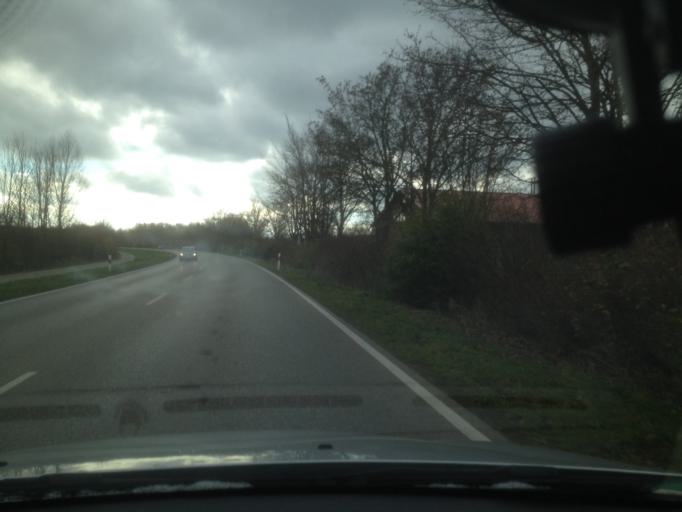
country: DE
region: Bavaria
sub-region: Swabia
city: Mering
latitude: 48.2647
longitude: 10.9694
